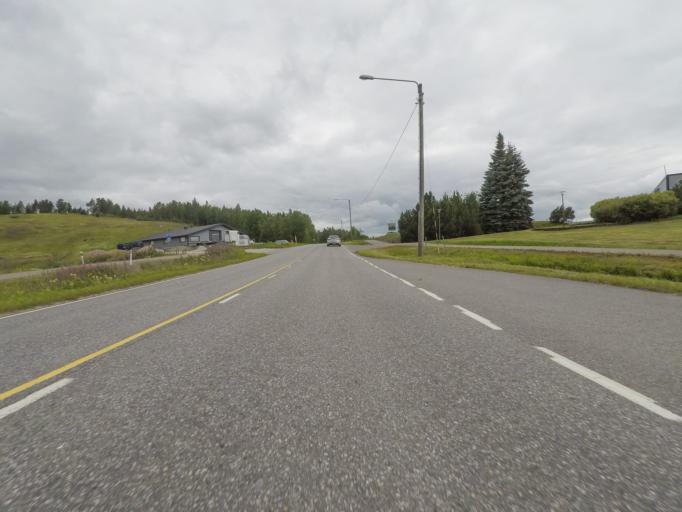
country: FI
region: Varsinais-Suomi
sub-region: Salo
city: Muurla
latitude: 60.3735
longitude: 23.3127
